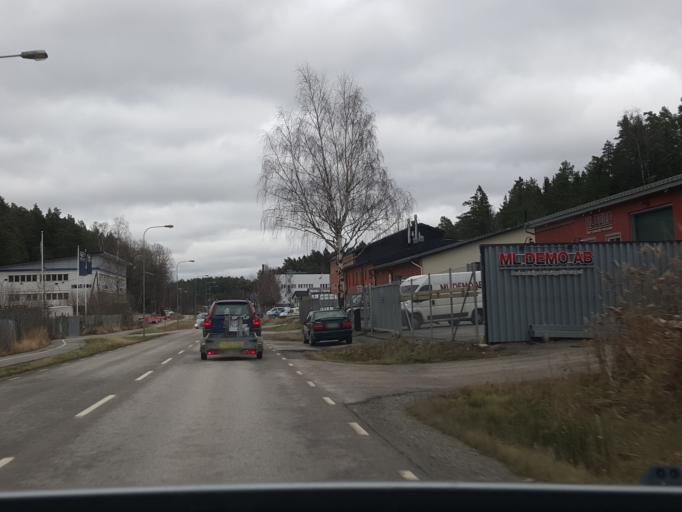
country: SE
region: Stockholm
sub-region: Nacka Kommun
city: Boo
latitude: 59.3247
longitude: 18.2675
